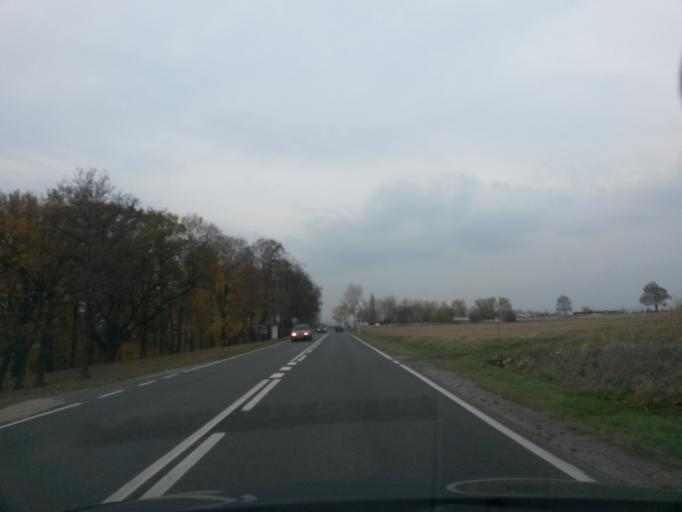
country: PL
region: Lower Silesian Voivodeship
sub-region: Powiat klodzki
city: Klodzko
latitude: 50.3874
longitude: 16.6614
